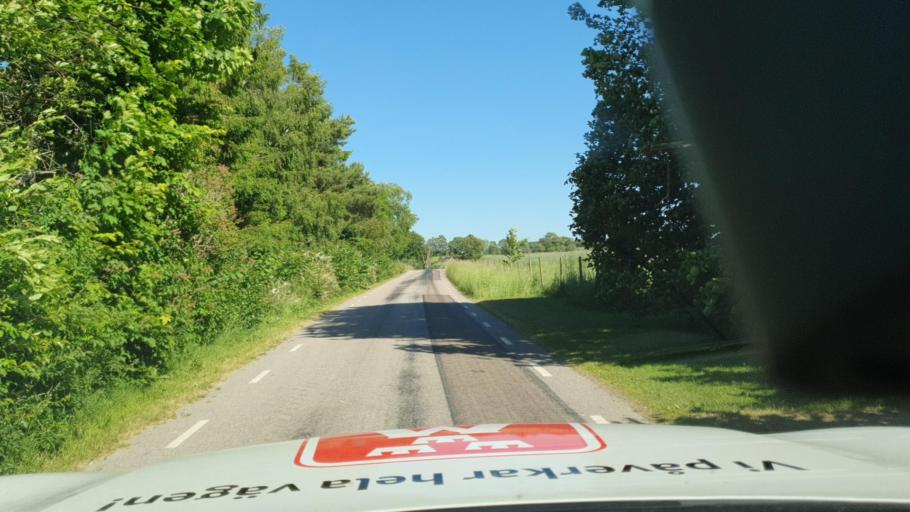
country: SE
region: Skane
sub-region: Sjobo Kommun
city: Sjoebo
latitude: 55.6326
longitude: 13.8270
